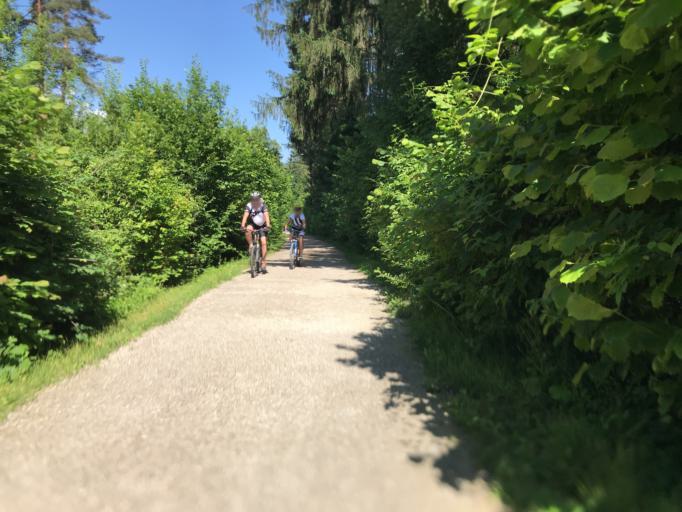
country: AT
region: Carinthia
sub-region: Villach Stadt
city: Villach
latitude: 46.5848
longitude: 13.8436
